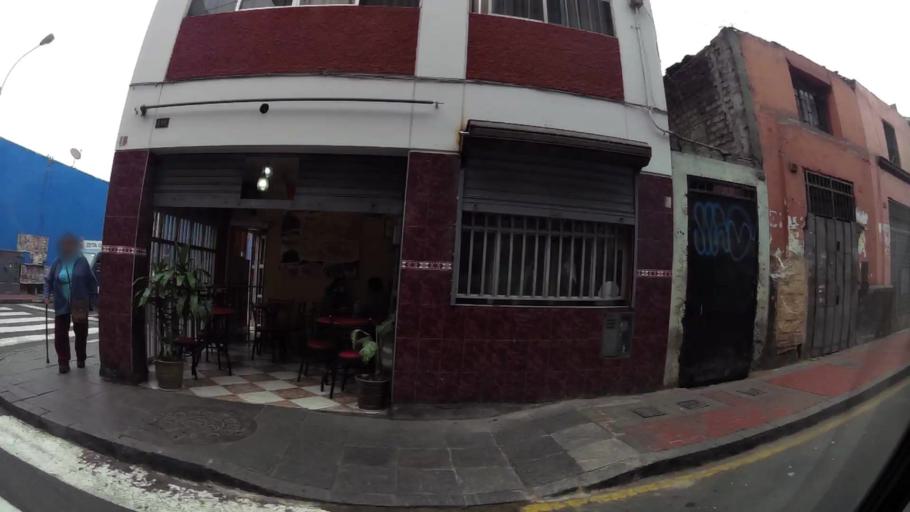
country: PE
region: Lima
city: Lima
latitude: -12.0442
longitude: -77.0343
